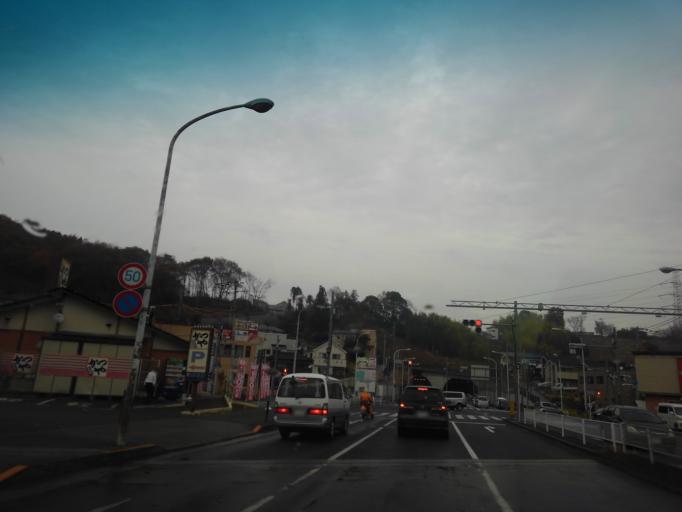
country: JP
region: Tokyo
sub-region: Machida-shi
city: Machida
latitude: 35.5878
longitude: 139.4504
